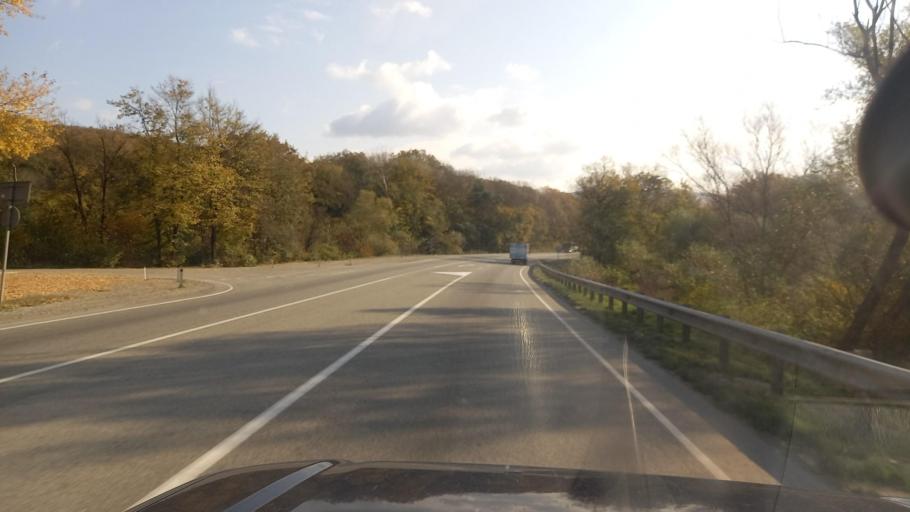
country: RU
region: Krasnodarskiy
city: Verkhnebakanskiy
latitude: 44.8434
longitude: 37.6951
